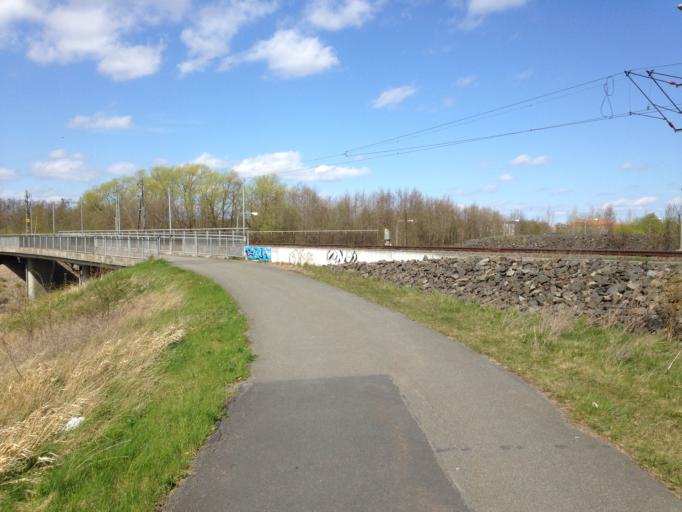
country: SE
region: Skane
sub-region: Kristianstads Kommun
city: Kristianstad
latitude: 56.0387
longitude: 14.1442
